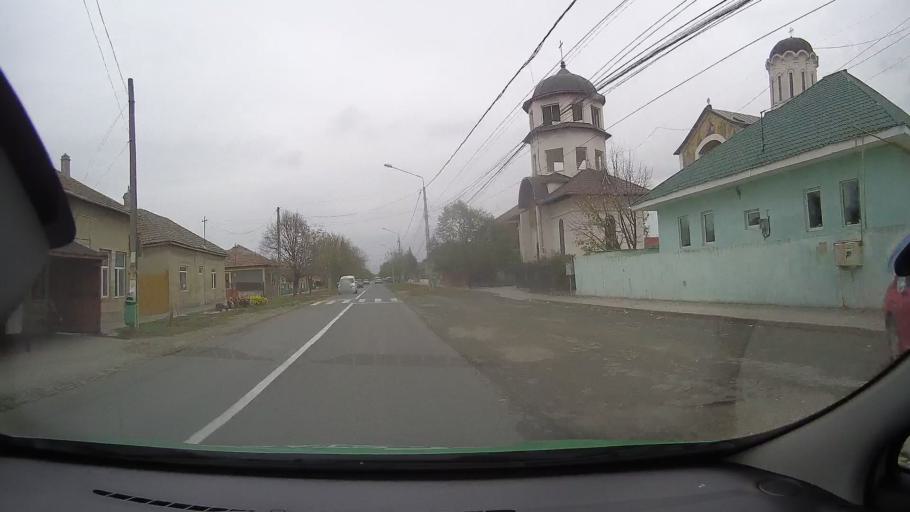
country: RO
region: Constanta
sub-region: Comuna Mihail Kogalniceanu
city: Mihail Kogalniceanu
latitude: 44.3692
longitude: 28.4630
